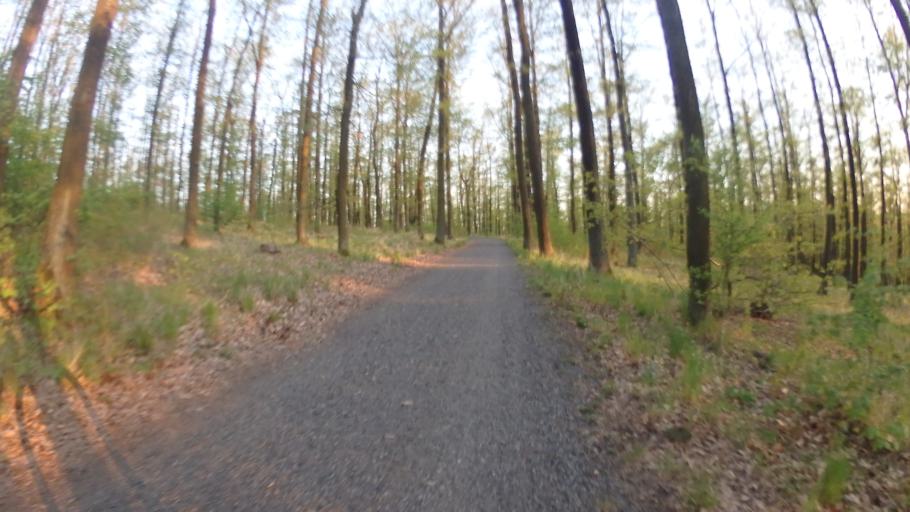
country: CZ
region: South Moravian
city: Troubsko
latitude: 49.1899
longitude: 16.5162
